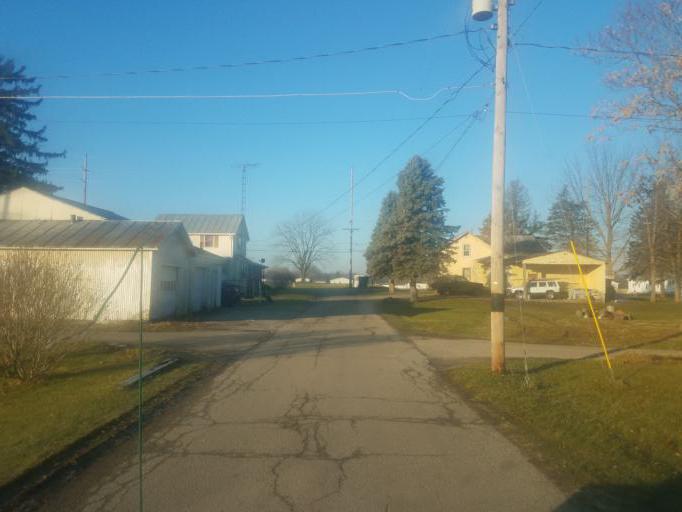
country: US
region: Ohio
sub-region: Crawford County
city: Bucyrus
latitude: 40.8210
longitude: -82.9809
